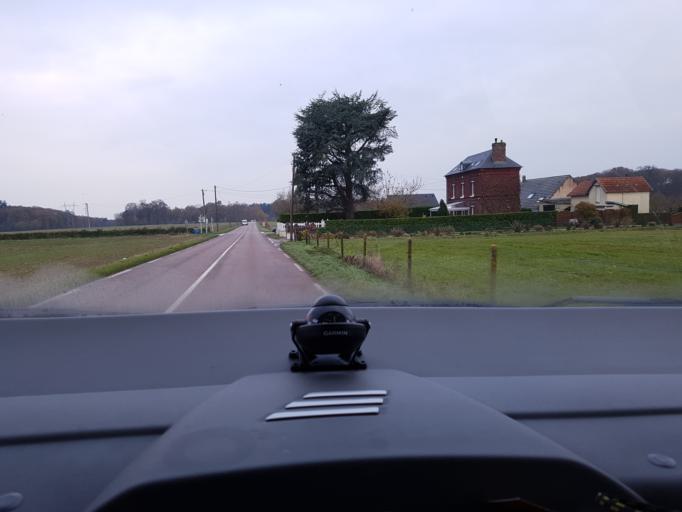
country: FR
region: Haute-Normandie
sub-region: Departement de la Seine-Maritime
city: Saint-Pierre-de-Varengeville
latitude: 49.4976
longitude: 0.9221
